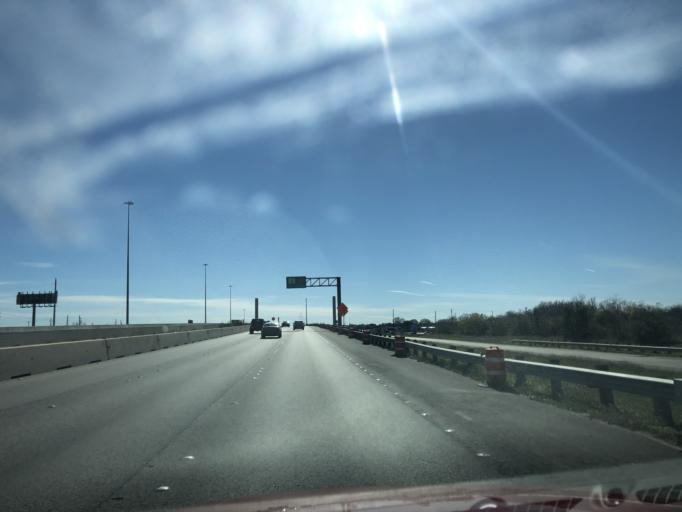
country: US
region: Texas
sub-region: Brazoria County
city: Brookside Village
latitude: 29.6173
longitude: -95.3873
